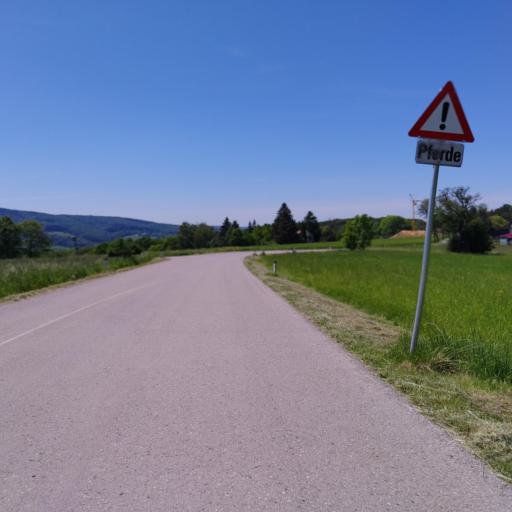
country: AT
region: Lower Austria
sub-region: Politischer Bezirk Sankt Polten
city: Maria-Anzbach
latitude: 48.2045
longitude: 15.9437
